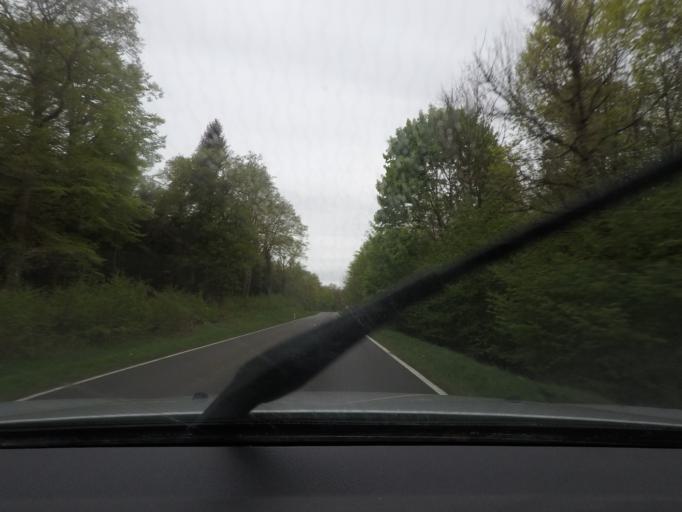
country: BE
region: Wallonia
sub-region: Province du Luxembourg
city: Virton
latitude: 49.6263
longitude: 5.5466
